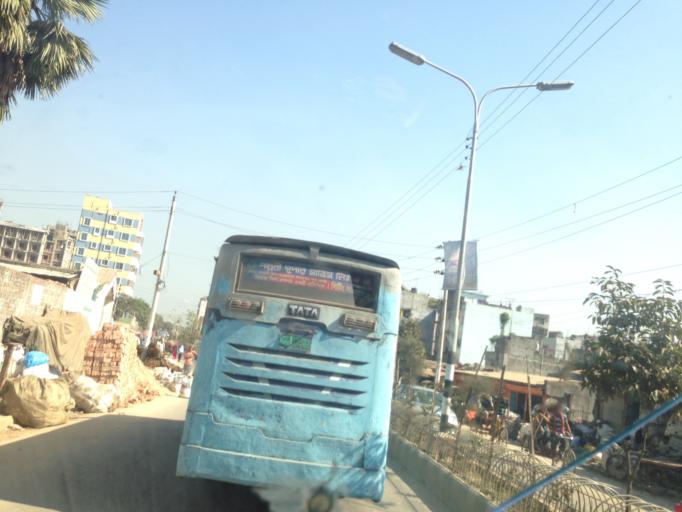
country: BD
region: Dhaka
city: Tungi
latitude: 23.8295
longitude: 90.3722
